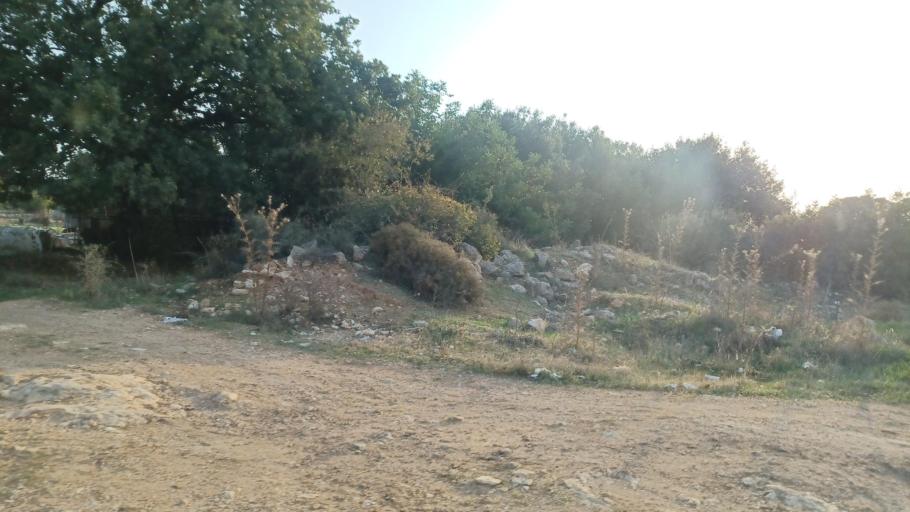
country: CY
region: Pafos
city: Polis
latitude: 34.9640
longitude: 32.4861
